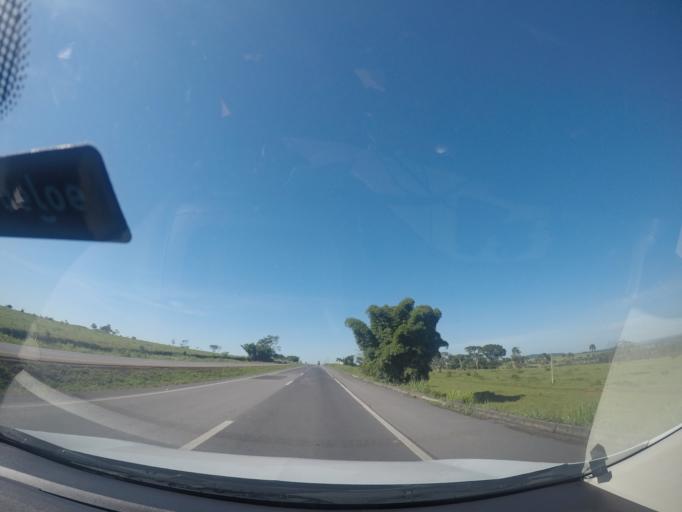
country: BR
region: Goias
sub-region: Pontalina
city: Pontalina
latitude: -17.5013
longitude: -49.2152
